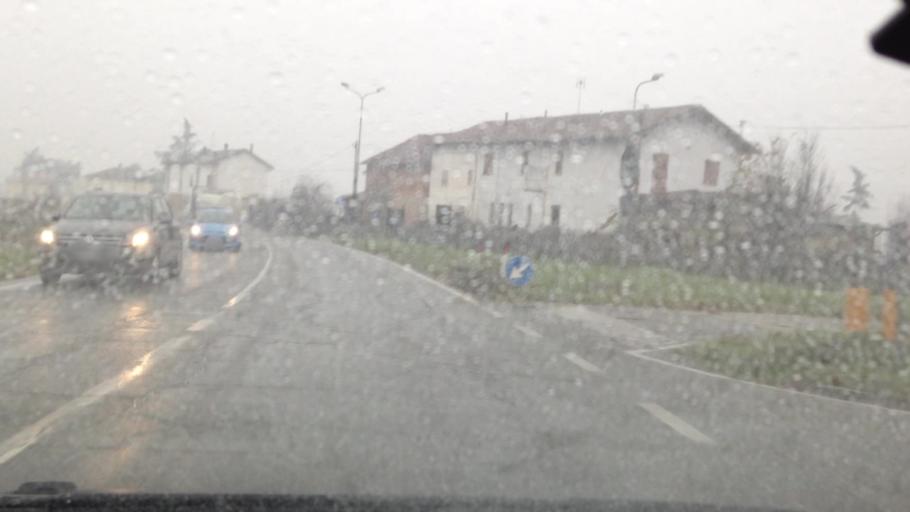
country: IT
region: Piedmont
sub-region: Provincia di Alessandria
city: Felizzano
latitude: 44.9001
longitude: 8.4440
